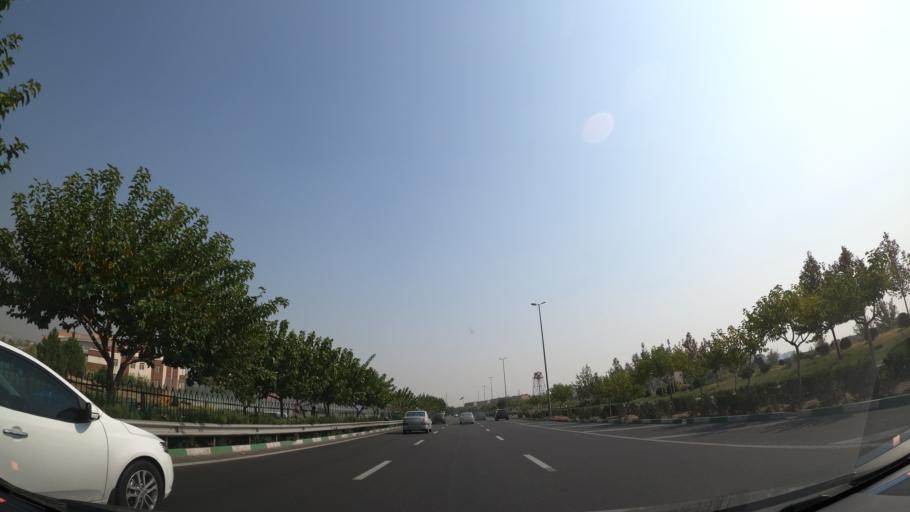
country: IR
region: Tehran
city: Shahr-e Qods
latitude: 35.7590
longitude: 51.2578
